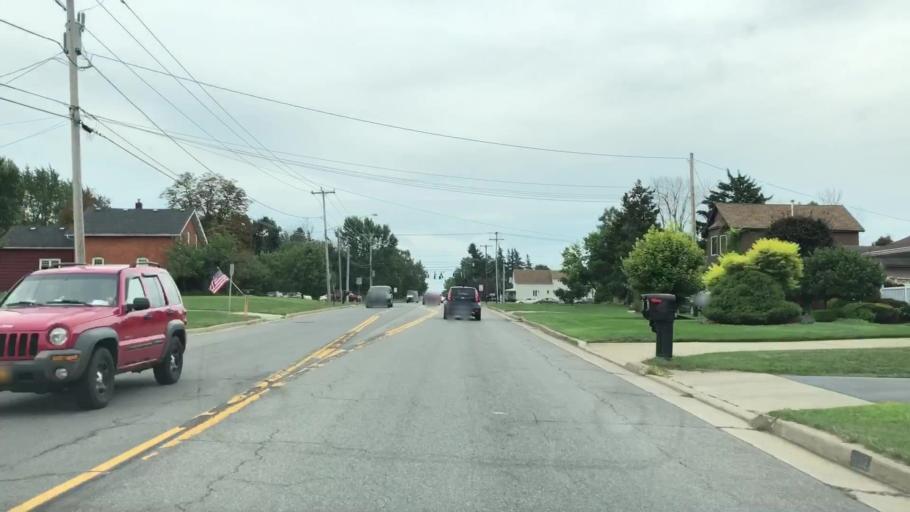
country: US
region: New York
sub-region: Erie County
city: Depew
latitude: 42.8814
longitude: -78.7091
